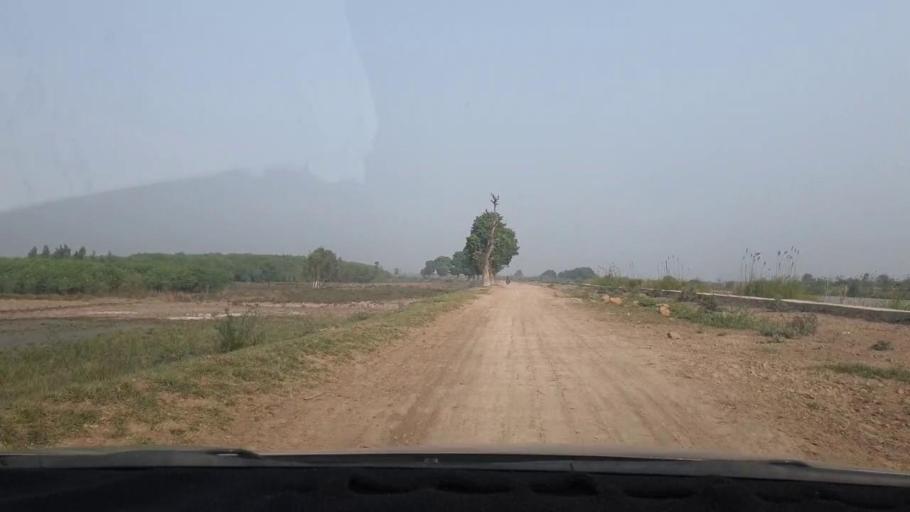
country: PK
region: Sindh
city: Matiari
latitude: 25.6496
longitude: 68.5612
